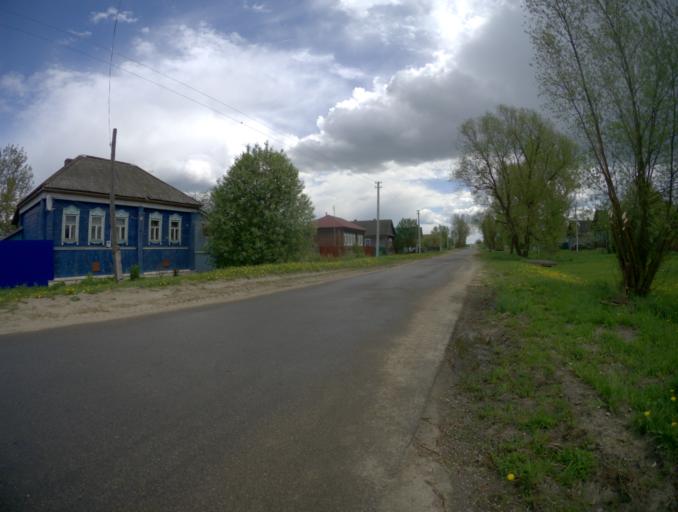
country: RU
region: Vladimir
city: Velikodvorskiy
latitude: 55.2687
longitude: 40.7929
